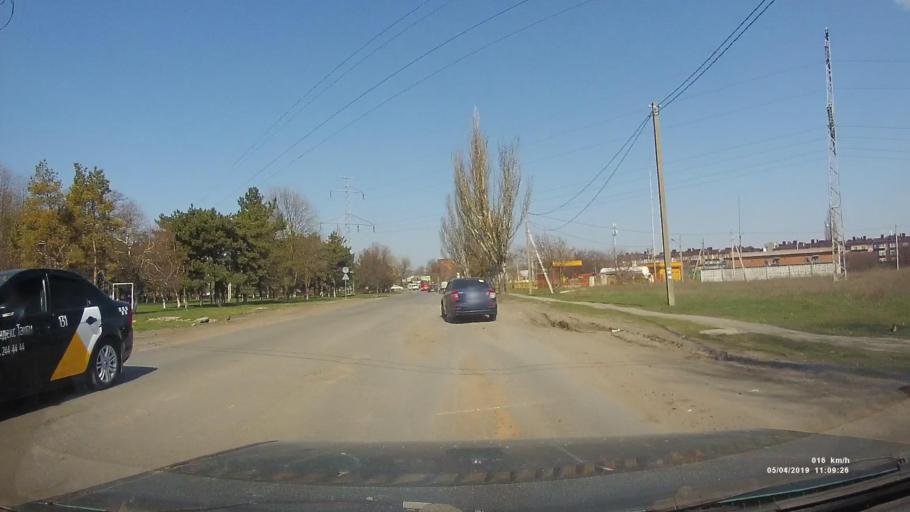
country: RU
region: Rostov
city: Azov
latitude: 47.0902
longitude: 39.4330
